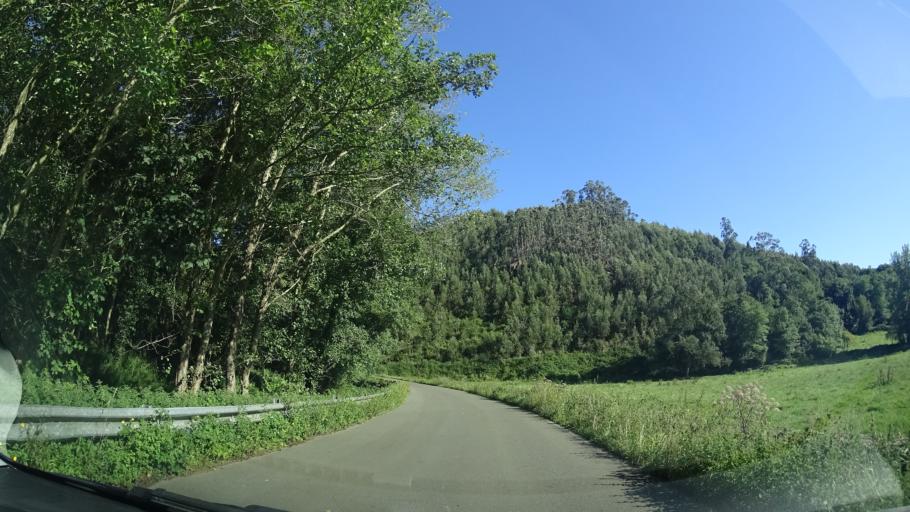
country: ES
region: Asturias
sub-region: Province of Asturias
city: Ribadesella
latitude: 43.4696
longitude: -5.1302
